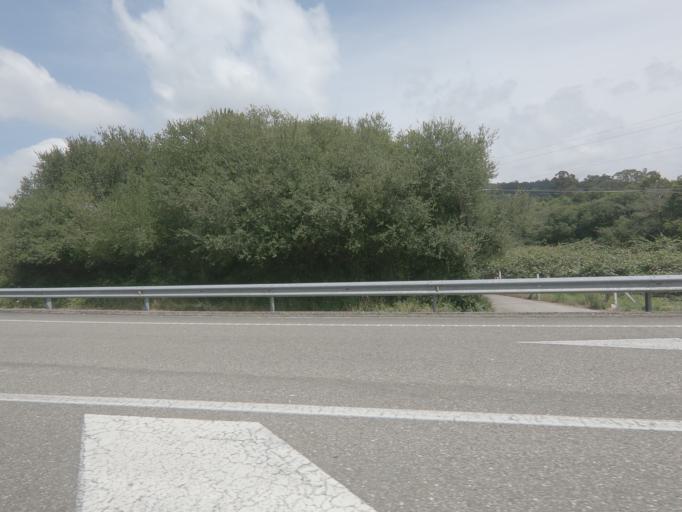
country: ES
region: Galicia
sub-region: Provincia de Pontevedra
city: Tomino
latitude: 42.0252
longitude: -8.7330
